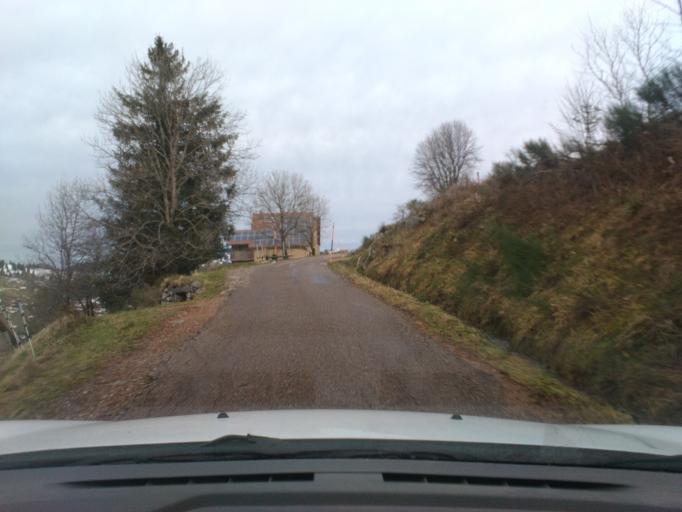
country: FR
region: Lorraine
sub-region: Departement des Vosges
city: La Bresse
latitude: 47.9914
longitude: 6.8729
